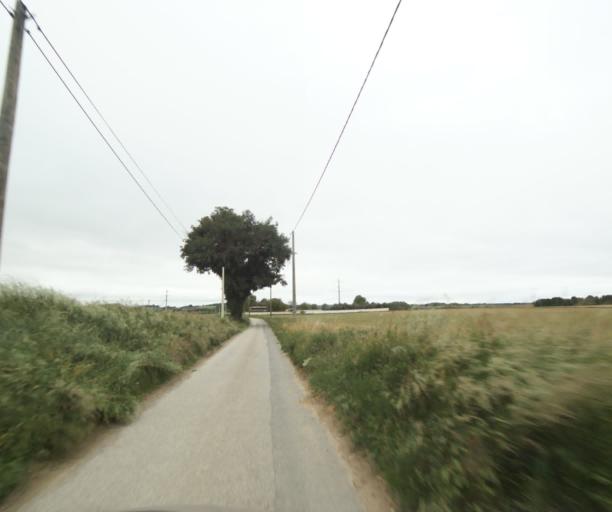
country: FR
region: Rhone-Alpes
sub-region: Departement du Rhone
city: Cailloux-sur-Fontaines
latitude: 45.8542
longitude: 4.9134
